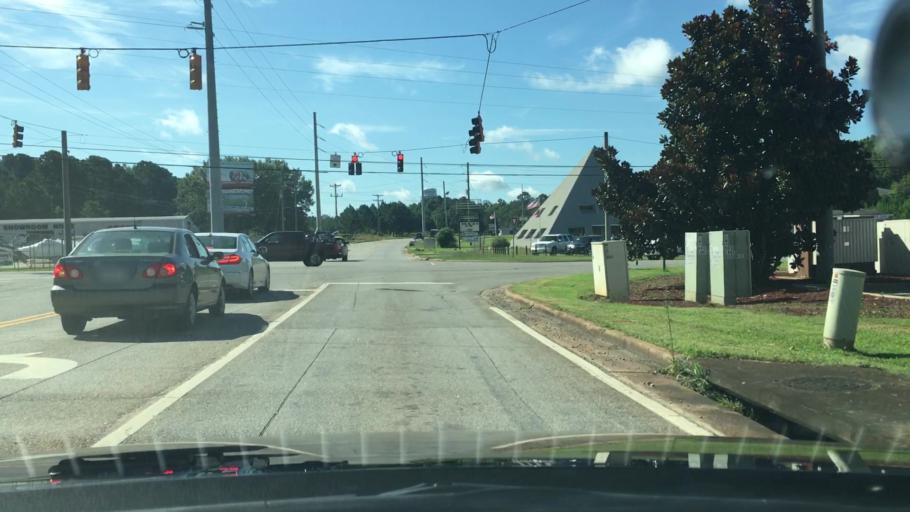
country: US
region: Georgia
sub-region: Putnam County
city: Jefferson
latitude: 33.4217
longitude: -83.2690
